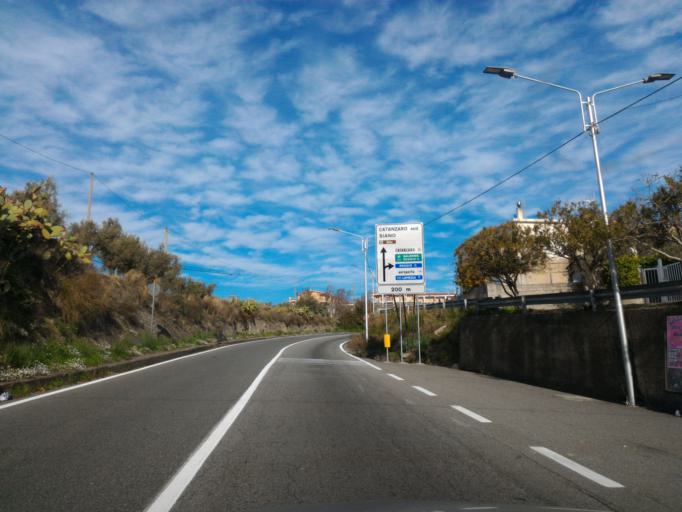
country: IT
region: Calabria
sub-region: Provincia di Catanzaro
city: Siano
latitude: 38.9100
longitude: 16.6015
